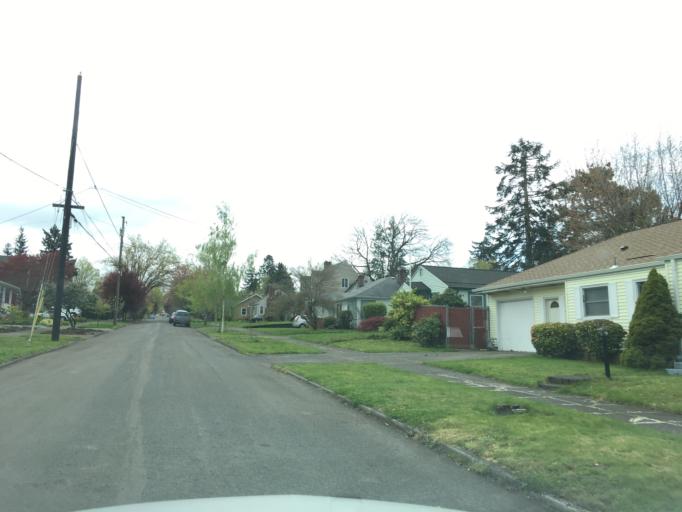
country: US
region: Oregon
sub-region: Multnomah County
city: Lents
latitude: 45.5554
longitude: -122.5922
